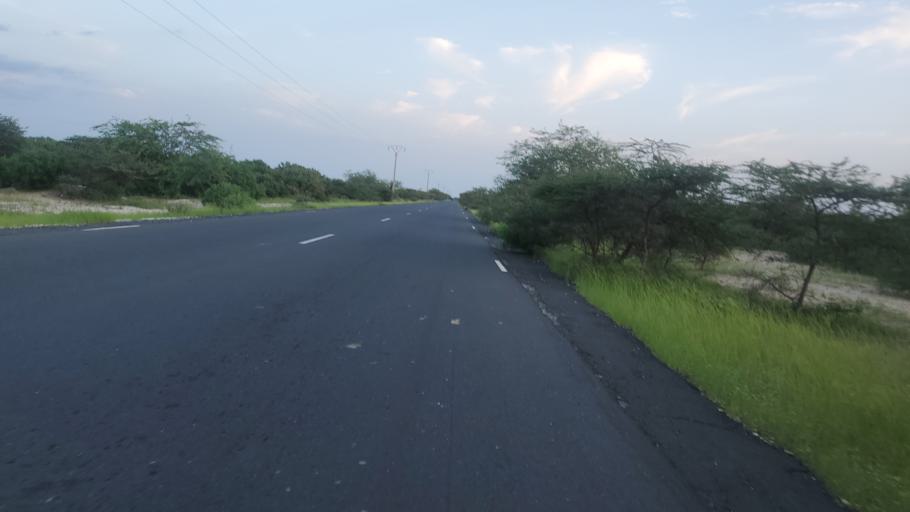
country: SN
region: Saint-Louis
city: Saint-Louis
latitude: 16.1153
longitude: -16.4134
